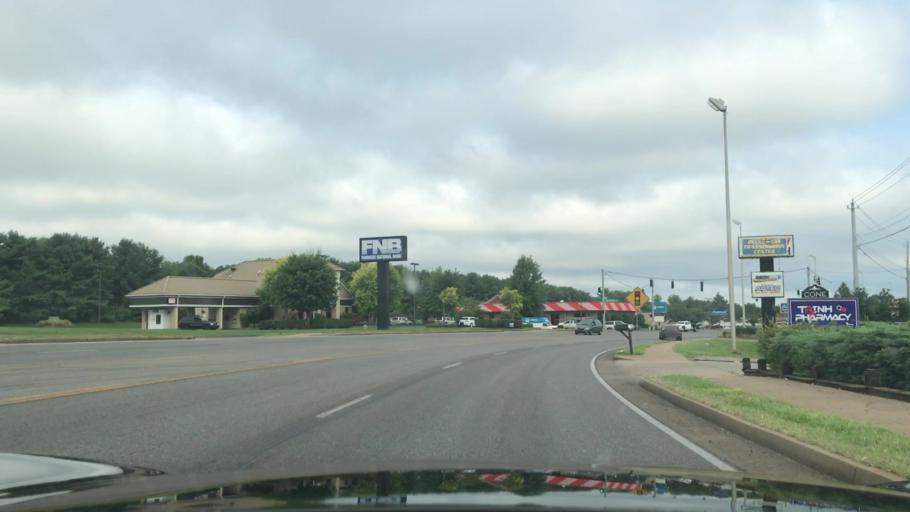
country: US
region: Kentucky
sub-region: Warren County
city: Bowling Green
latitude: 36.9510
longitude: -86.4402
